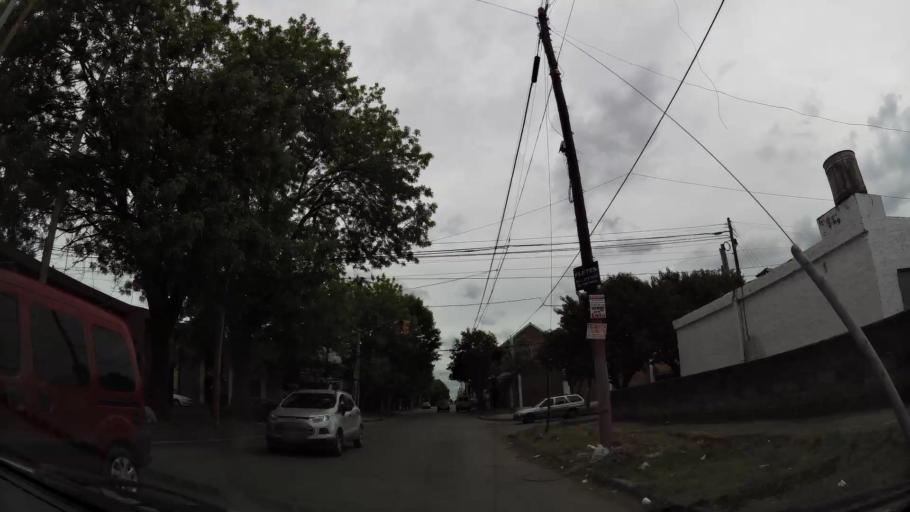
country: AR
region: Buenos Aires
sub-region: Partido de Quilmes
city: Quilmes
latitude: -34.7645
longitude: -58.2644
